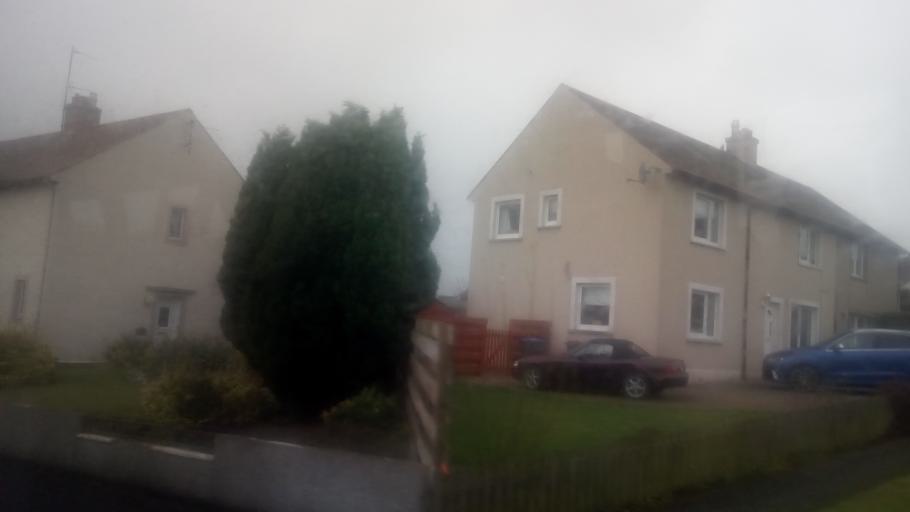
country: GB
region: Scotland
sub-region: The Scottish Borders
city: Jedburgh
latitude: 55.5134
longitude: -2.5857
